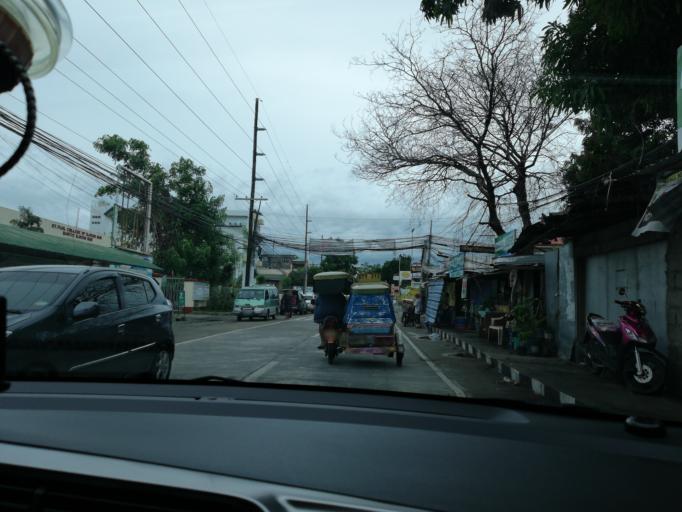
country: PH
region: Ilocos
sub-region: Province of Ilocos Sur
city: Vigan
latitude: 17.5796
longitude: 120.3866
